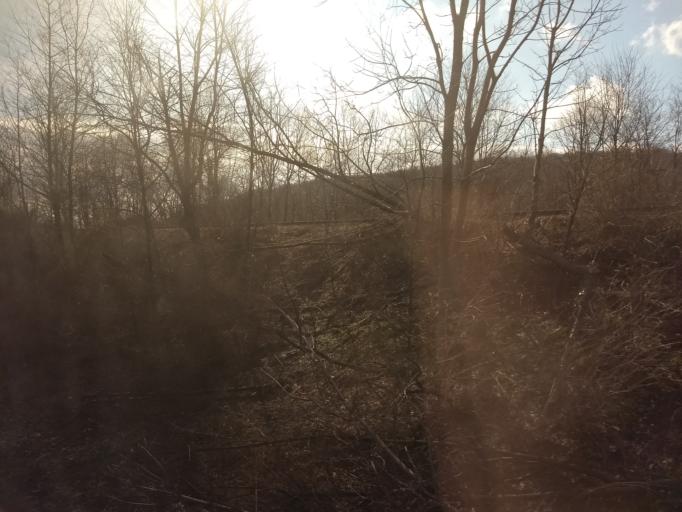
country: US
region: Pennsylvania
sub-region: Cambria County
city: Gallitzin
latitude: 40.4788
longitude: -78.5285
